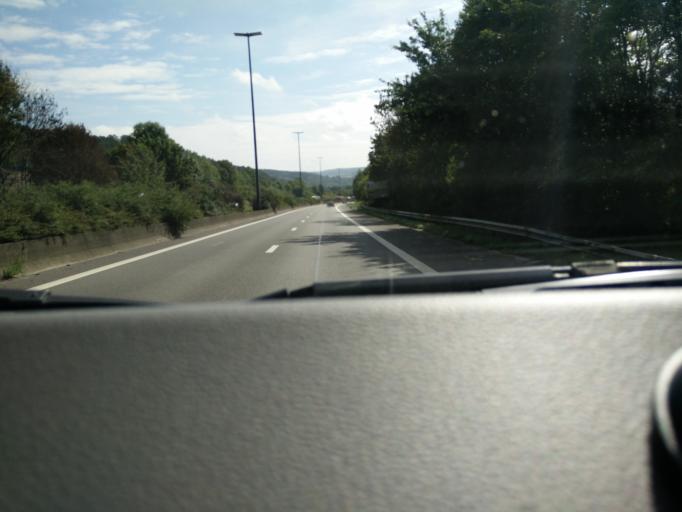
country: BE
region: Wallonia
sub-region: Province du Luxembourg
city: Wellin
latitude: 50.0920
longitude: 5.1505
